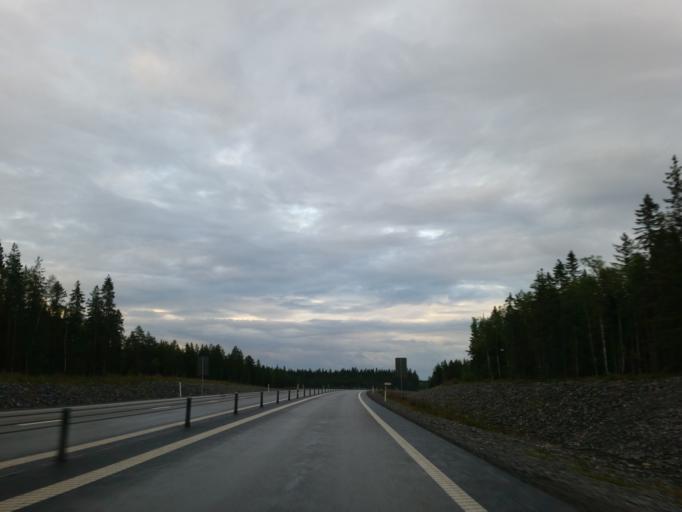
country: SE
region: Vaesterbotten
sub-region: Umea Kommun
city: Umea
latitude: 63.8581
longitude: 20.2431
